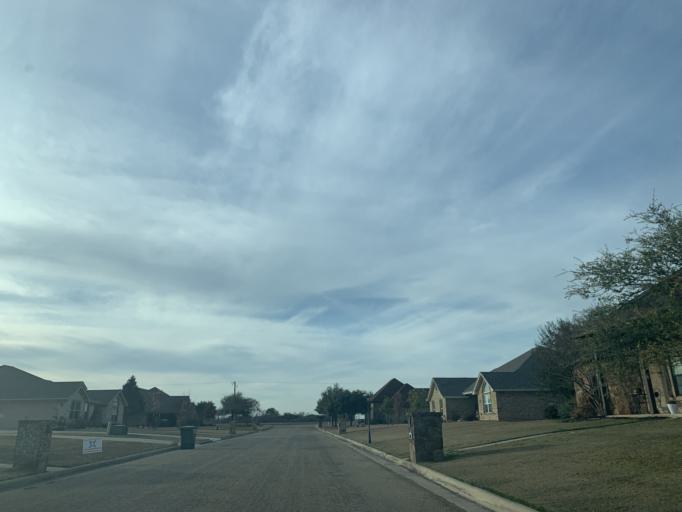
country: US
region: Texas
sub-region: Bell County
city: Salado
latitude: 30.9701
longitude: -97.5126
